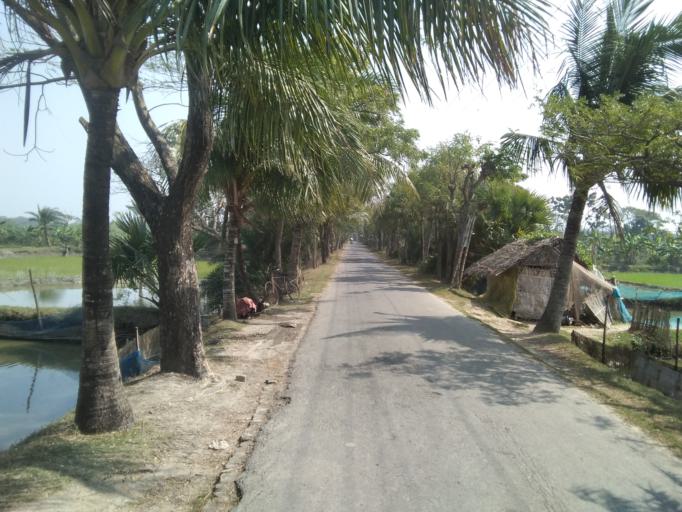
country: IN
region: West Bengal
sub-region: North 24 Parganas
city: Taki
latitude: 22.5927
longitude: 88.9893
